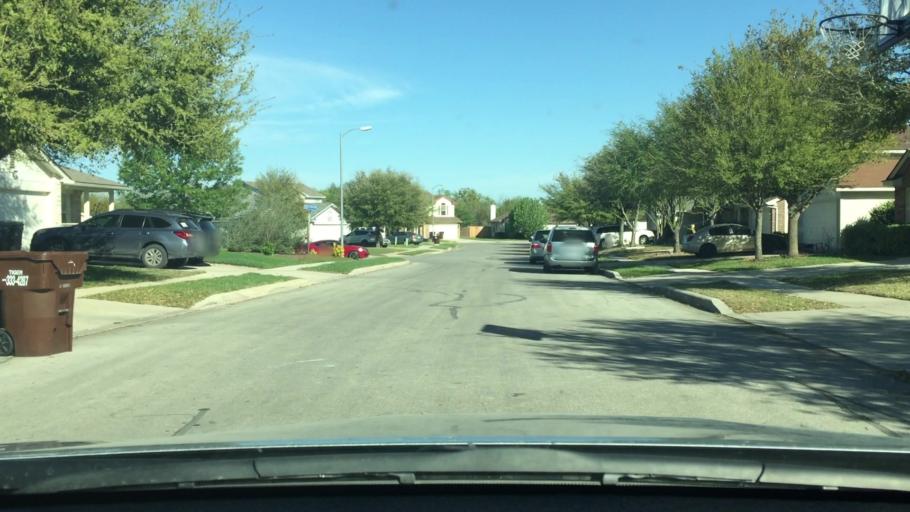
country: US
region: Texas
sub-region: Bexar County
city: Converse
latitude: 29.4662
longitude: -98.3220
